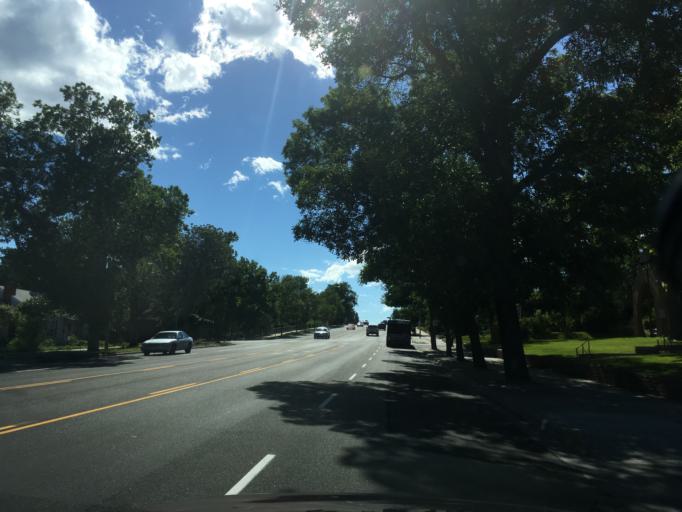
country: US
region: Montana
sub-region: Yellowstone County
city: Billings
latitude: 45.7841
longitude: -108.5295
